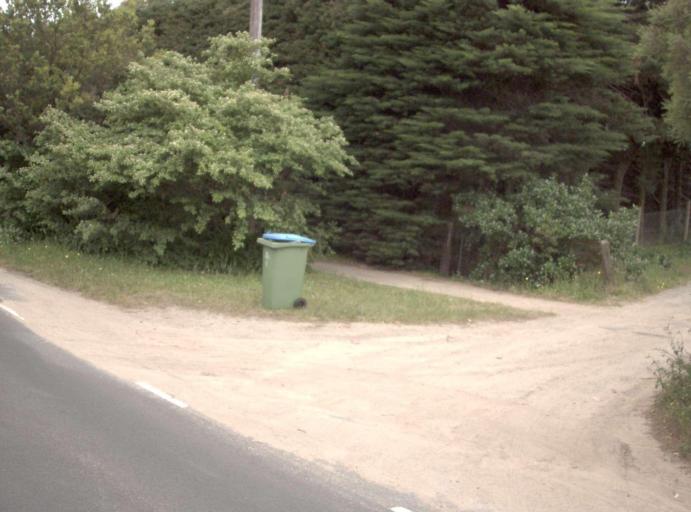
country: AU
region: Victoria
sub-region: Mornington Peninsula
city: Sorrento
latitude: -38.3260
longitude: 144.7351
